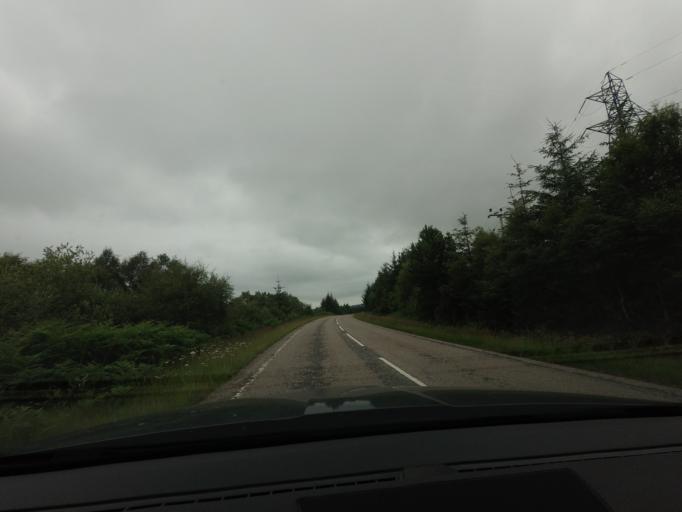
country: GB
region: Scotland
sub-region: Highland
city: Alness
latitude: 57.9928
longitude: -4.4040
